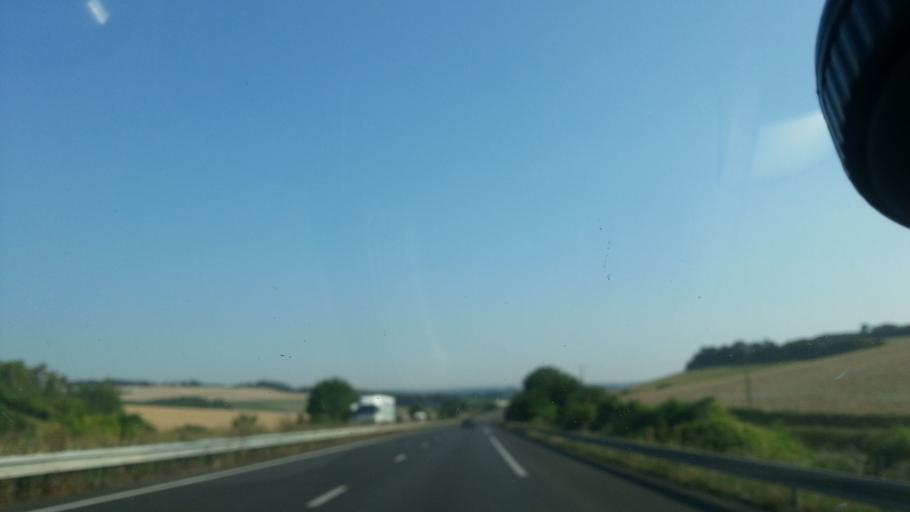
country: FR
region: Poitou-Charentes
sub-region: Departement de la Vienne
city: Les Ormes
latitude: 46.9904
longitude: 0.5492
